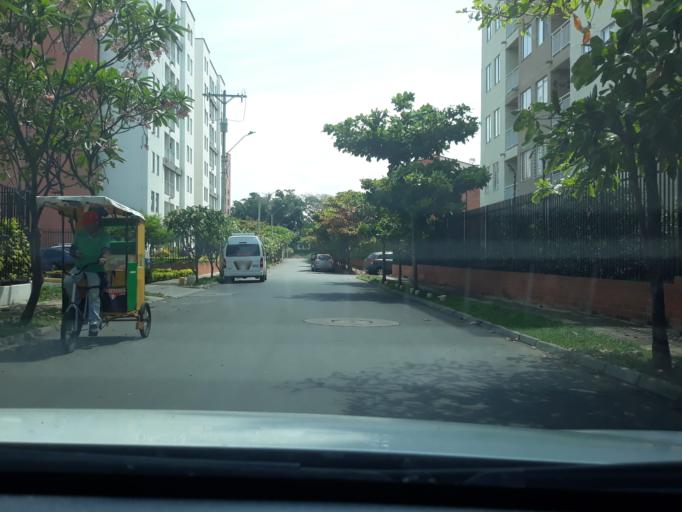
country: CO
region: Valle del Cauca
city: Cali
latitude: 3.3709
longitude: -76.5111
